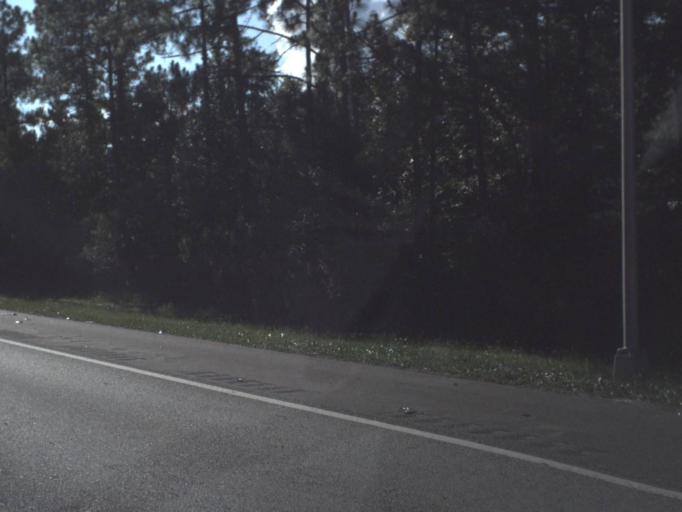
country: US
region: Florida
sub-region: Duval County
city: Jacksonville
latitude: 30.2501
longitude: -81.5656
